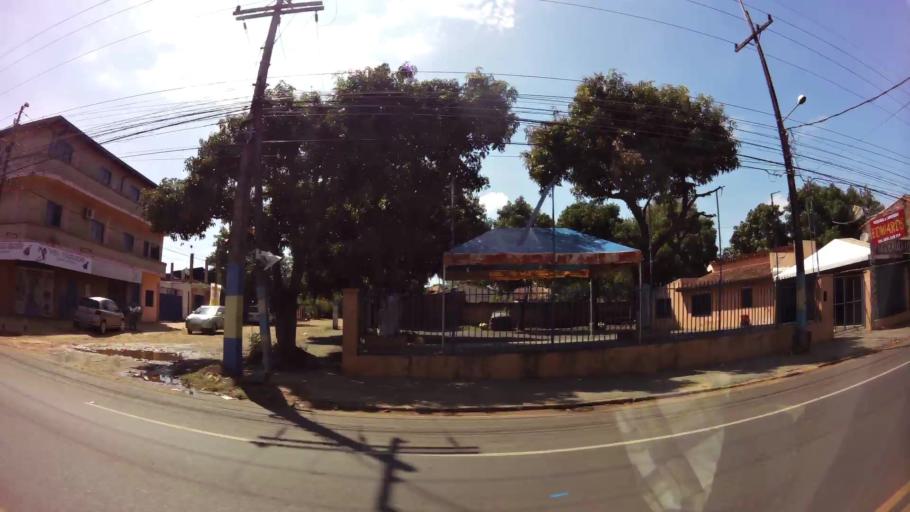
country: PY
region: Central
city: San Lorenzo
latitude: -25.3037
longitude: -57.5044
